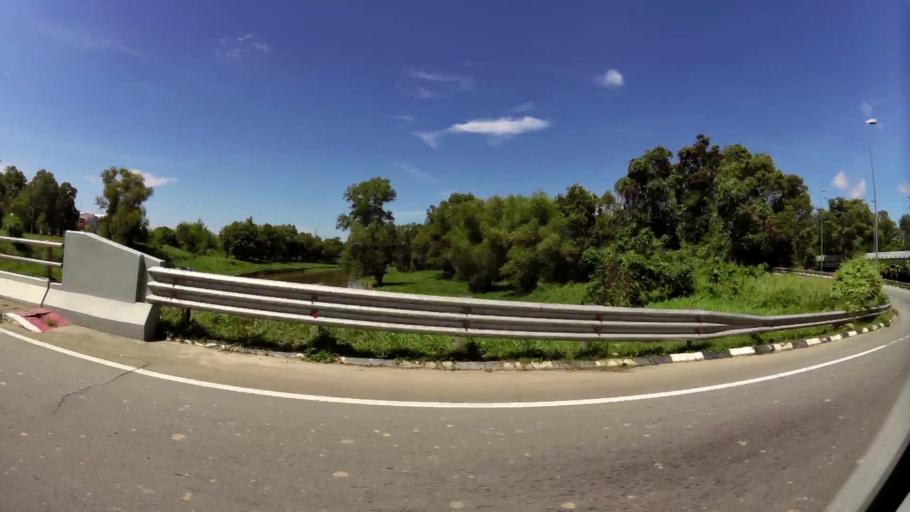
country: BN
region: Brunei and Muara
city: Bandar Seri Begawan
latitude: 4.9428
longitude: 114.9381
